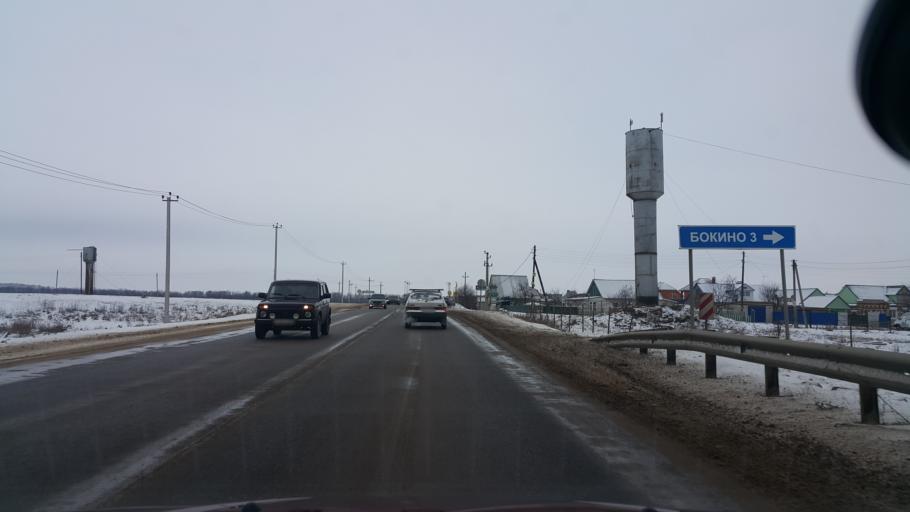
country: RU
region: Tambov
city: Bokino
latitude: 52.6163
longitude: 41.4616
